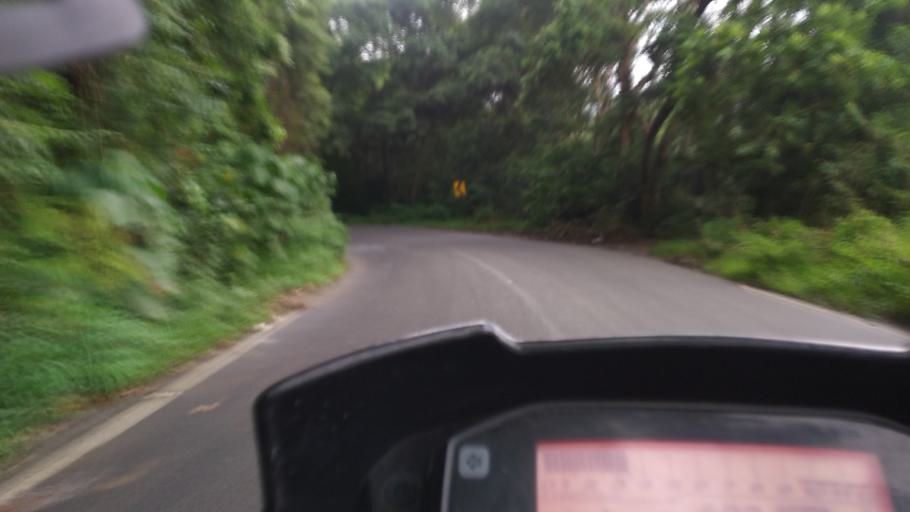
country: IN
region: Kerala
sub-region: Idukki
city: Kuttampuzha
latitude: 10.0656
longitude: 76.7848
